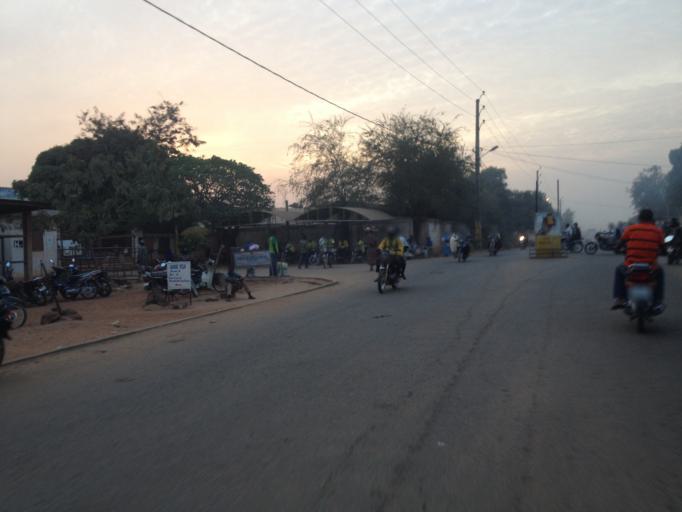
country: BJ
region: Borgou
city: Parakou
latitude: 9.3369
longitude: 2.6369
